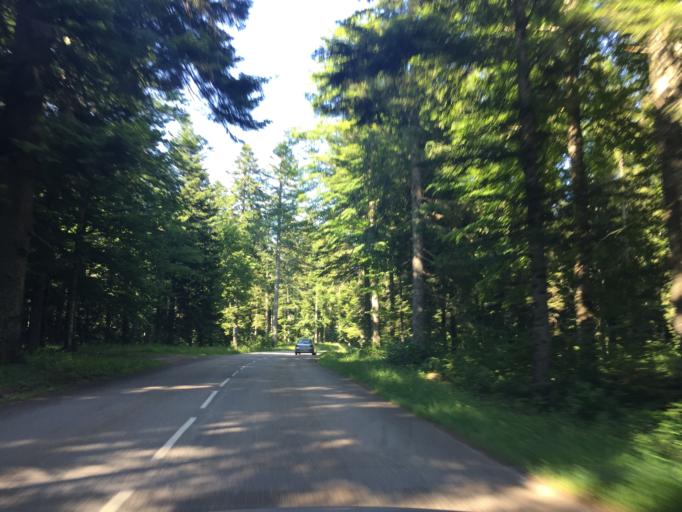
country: FR
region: Rhone-Alpes
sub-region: Departement de la Drome
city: Saint-Jean-en-Royans
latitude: 44.9377
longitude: 5.3075
